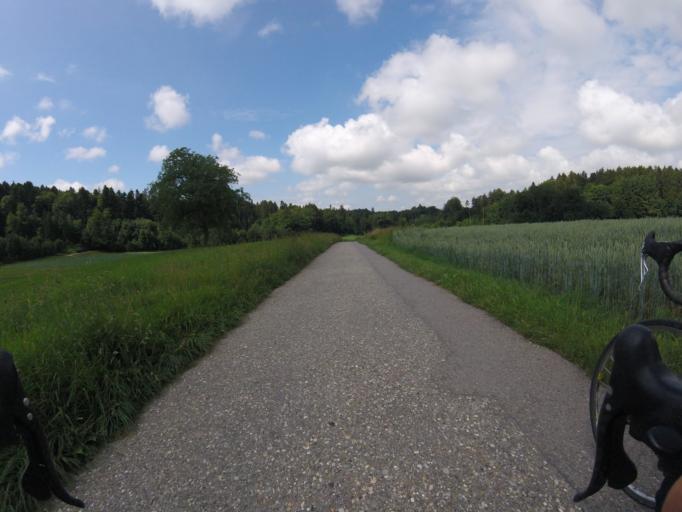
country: CH
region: Bern
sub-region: Bern-Mittelland District
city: Bariswil
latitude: 47.0169
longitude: 7.5193
